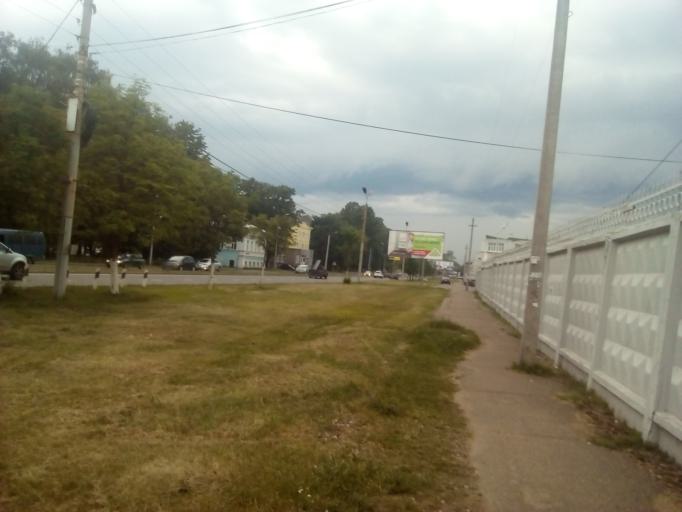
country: RU
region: Jaroslavl
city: Yaroslavl
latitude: 57.6084
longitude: 39.8557
